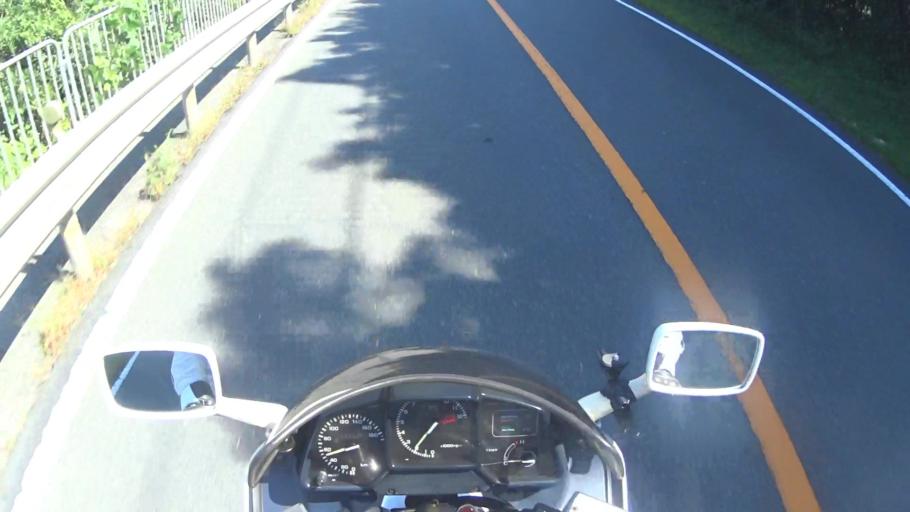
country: JP
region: Kyoto
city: Kameoka
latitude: 34.9531
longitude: 135.5052
